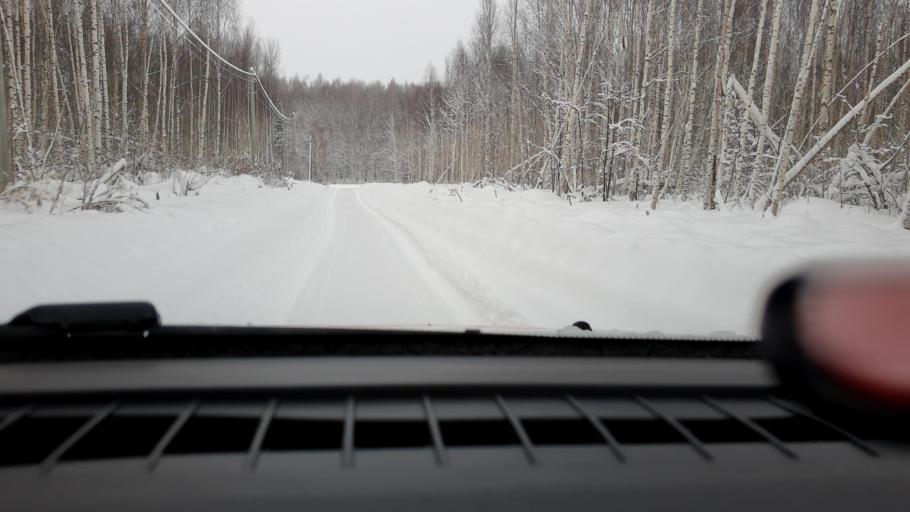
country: RU
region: Nizjnij Novgorod
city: Afonino
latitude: 56.1311
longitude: 43.9720
